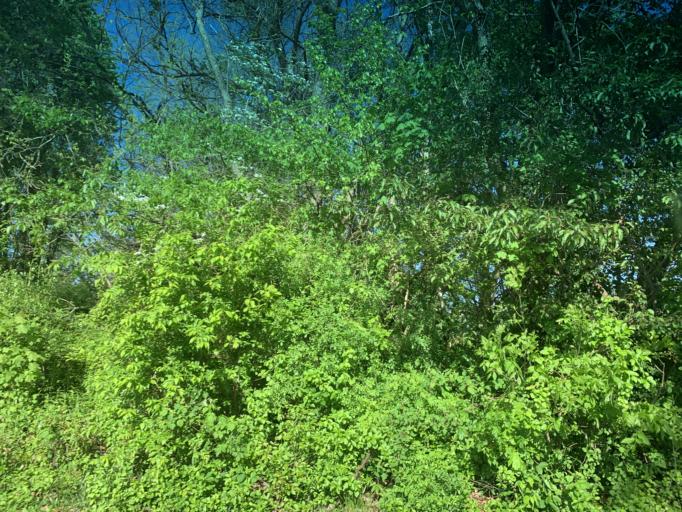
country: US
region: Maryland
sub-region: Harford County
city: Aberdeen
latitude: 39.5378
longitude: -76.2068
